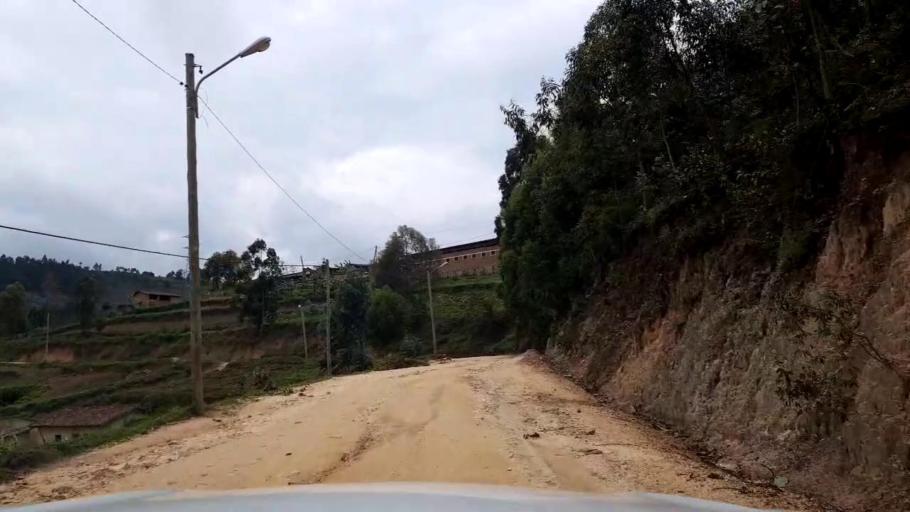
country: RW
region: Western Province
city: Kibuye
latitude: -1.9672
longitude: 29.3915
